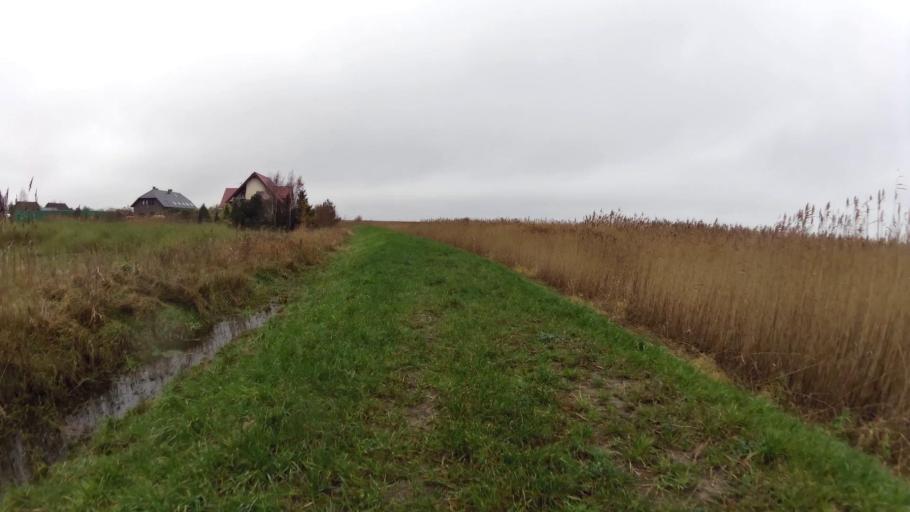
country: PL
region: West Pomeranian Voivodeship
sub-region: Powiat koszalinski
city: Mielno
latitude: 54.2587
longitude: 16.1037
